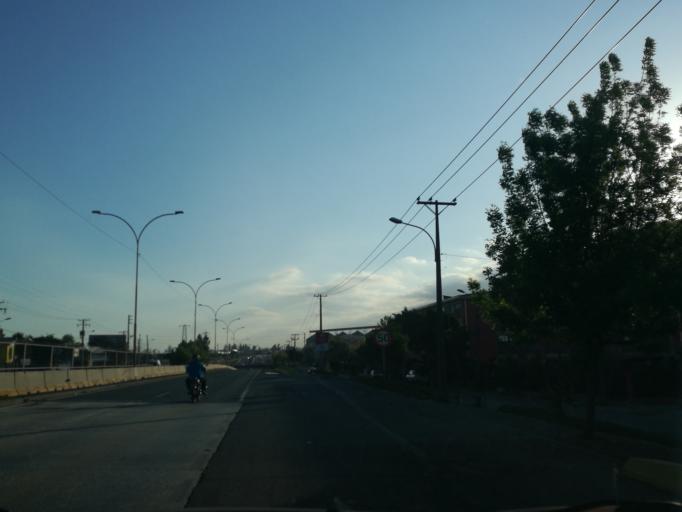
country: CL
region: O'Higgins
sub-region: Provincia de Cachapoal
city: Rancagua
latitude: -34.1821
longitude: -70.7375
